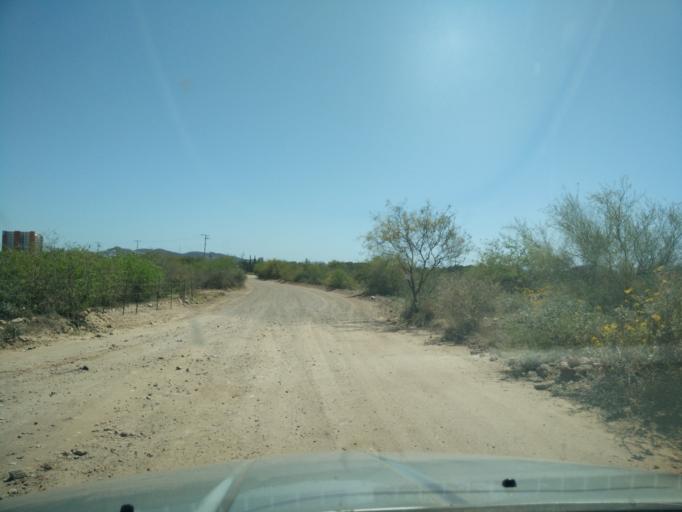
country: MX
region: Sonora
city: Heroica Guaymas
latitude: 27.9755
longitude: -111.1122
